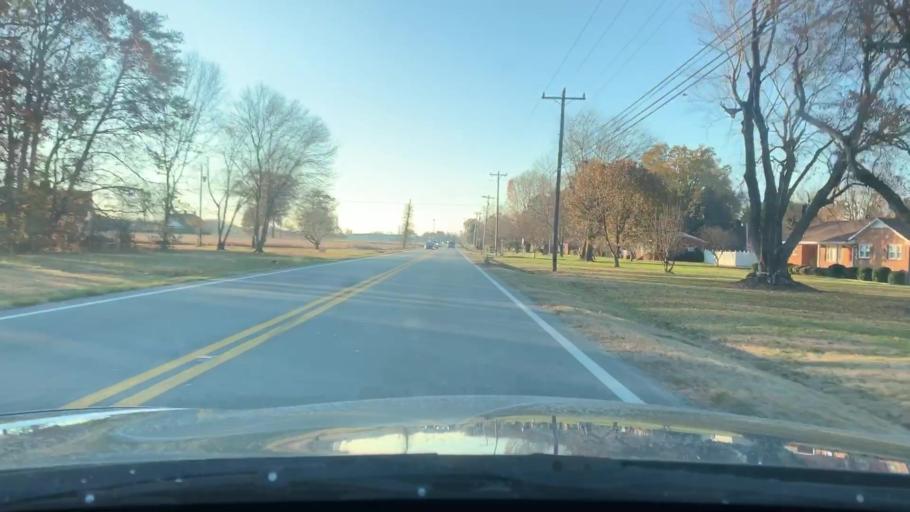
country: US
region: North Carolina
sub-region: Alamance County
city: Green Level
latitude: 36.1106
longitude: -79.3535
